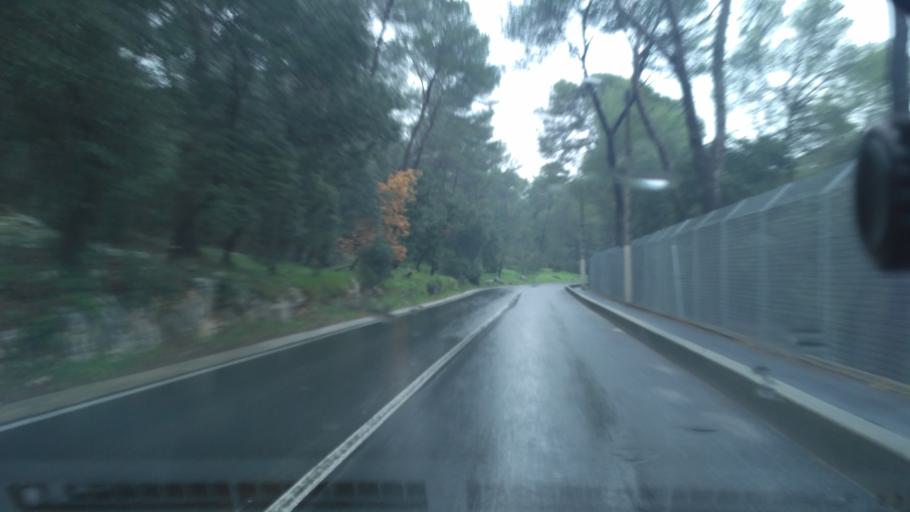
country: FR
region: Languedoc-Roussillon
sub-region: Departement de l'Herault
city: Clapiers
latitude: 43.6414
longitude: 3.8720
